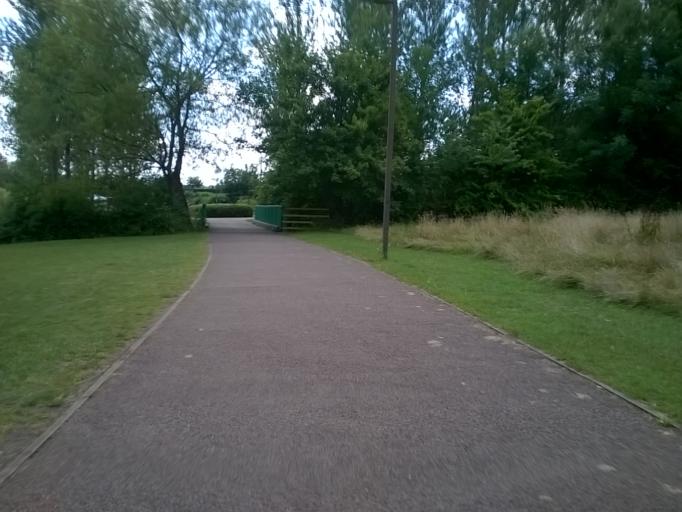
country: GB
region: England
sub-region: Milton Keynes
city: Broughton
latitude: 52.0529
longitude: -0.7251
